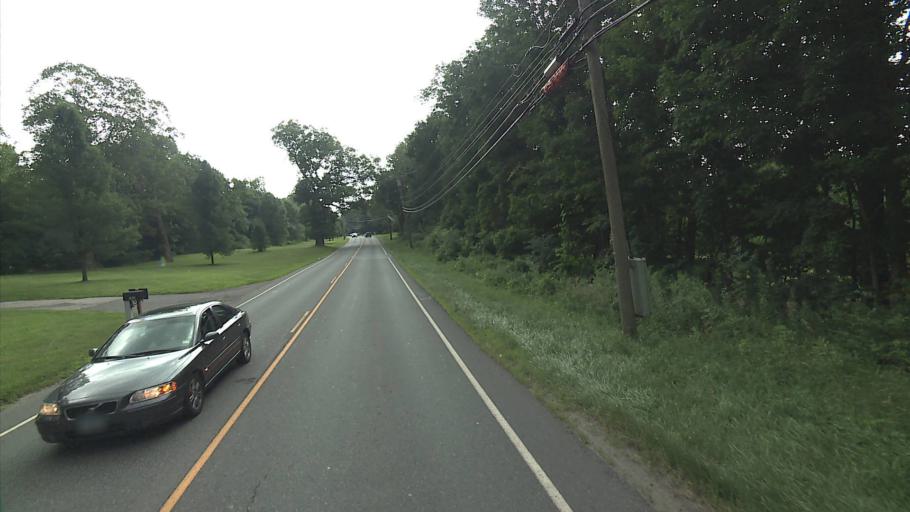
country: US
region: Connecticut
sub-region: New Haven County
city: Southbury
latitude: 41.4909
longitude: -73.2131
